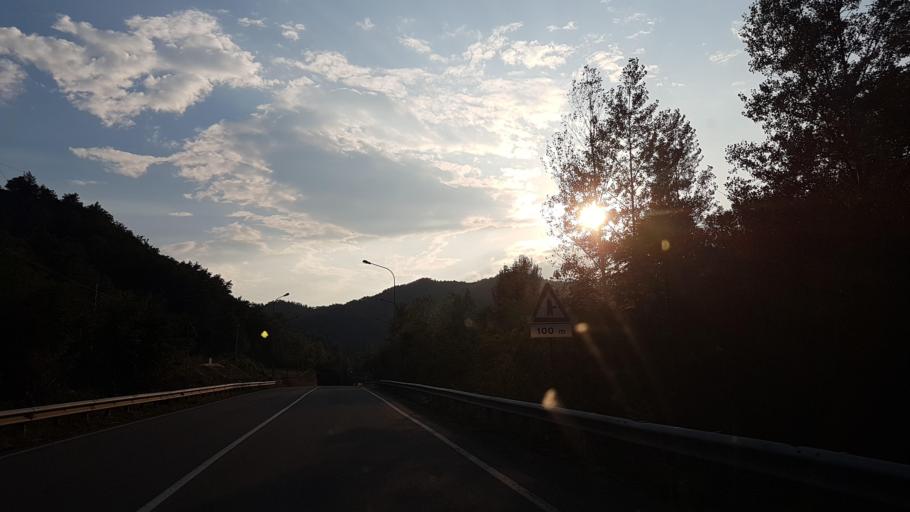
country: IT
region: Emilia-Romagna
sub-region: Provincia di Parma
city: Stazione Valmozzola
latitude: 44.5309
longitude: 9.8712
